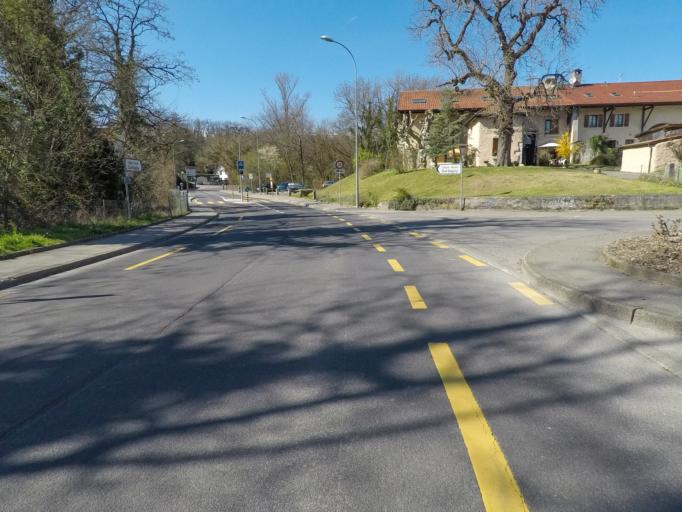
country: CH
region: Geneva
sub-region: Geneva
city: Aire-la-Ville
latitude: 46.2006
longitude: 6.0442
